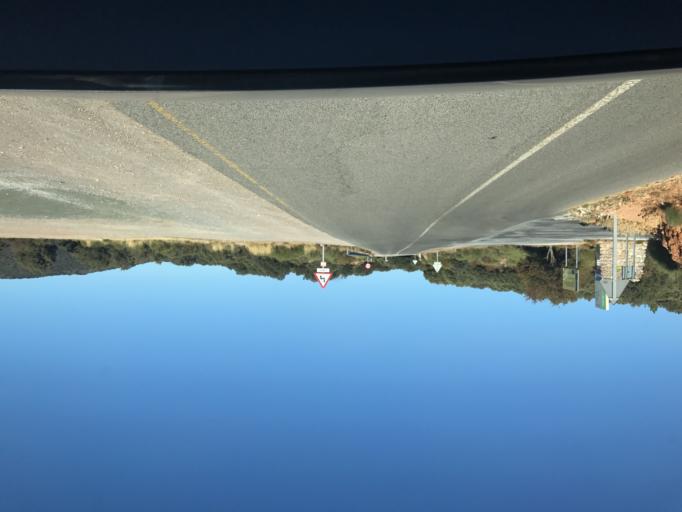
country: ES
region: Andalusia
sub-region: Provincia de Granada
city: Beas de Granada
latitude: 37.3021
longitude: -3.4432
